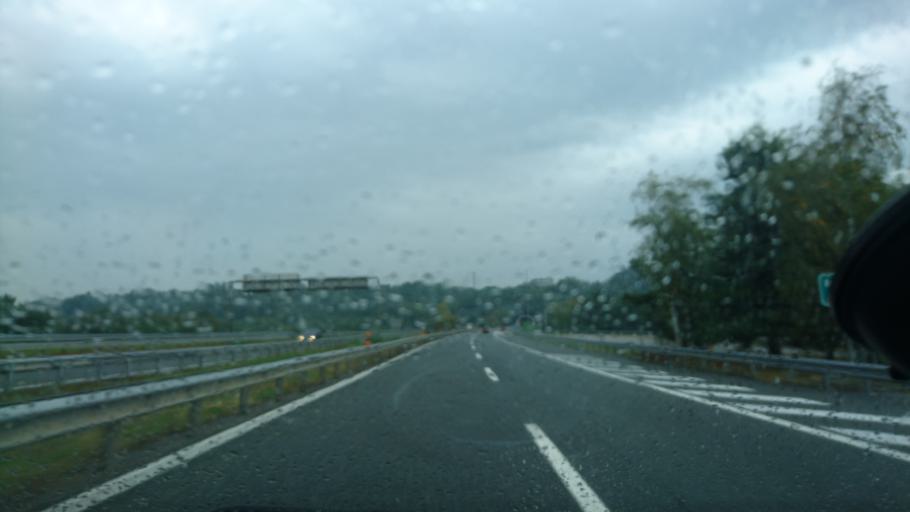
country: IT
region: Piedmont
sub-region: Provincia di Novara
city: Ghemme
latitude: 45.6109
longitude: 8.4110
